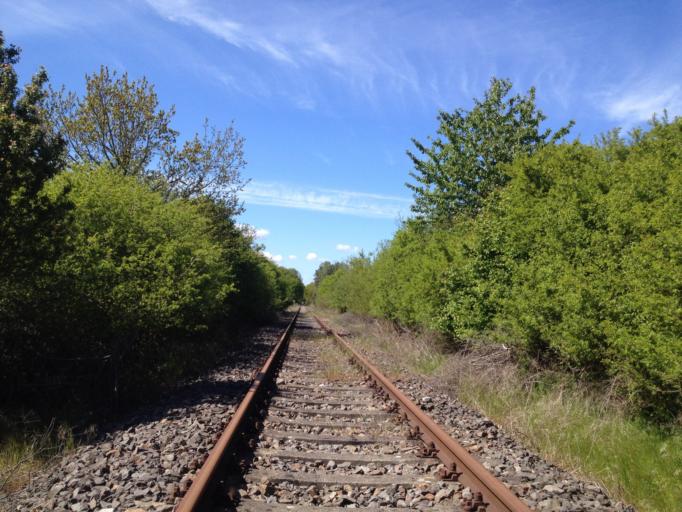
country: DE
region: Brandenburg
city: Templin
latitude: 53.1217
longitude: 13.4503
